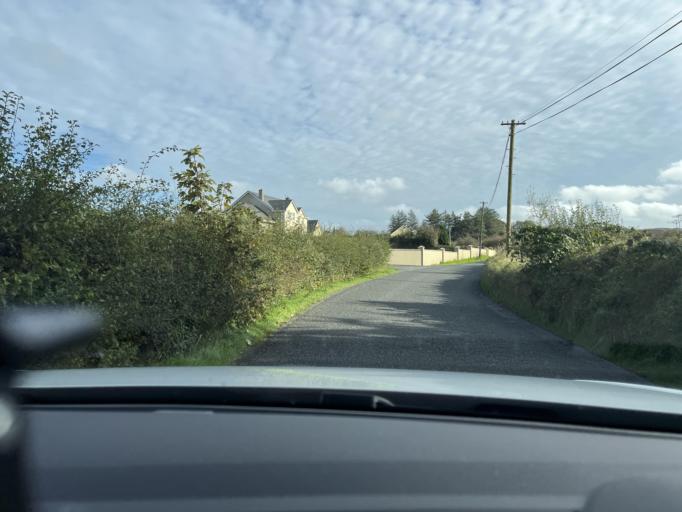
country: IE
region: Connaught
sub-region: Sligo
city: Ballymote
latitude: 54.0788
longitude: -8.4137
